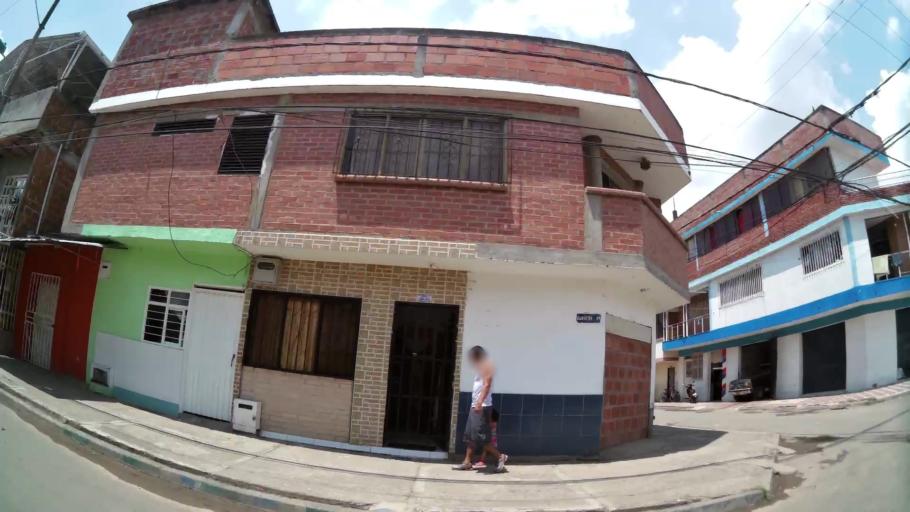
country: CO
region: Valle del Cauca
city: Cali
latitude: 3.4493
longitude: -76.4778
